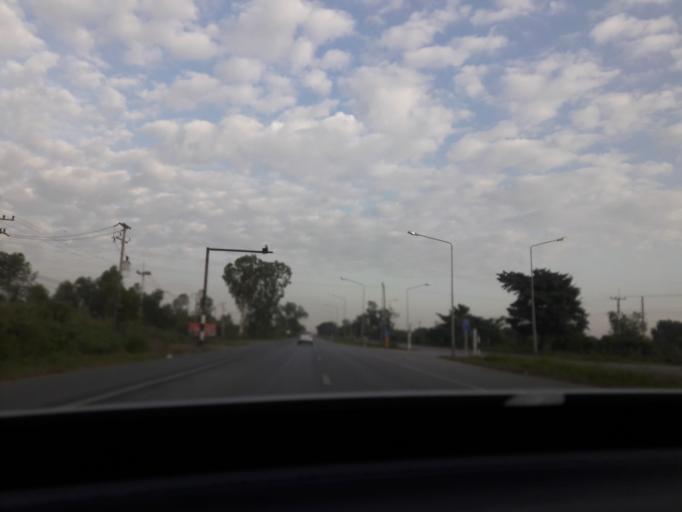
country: TH
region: Phra Nakhon Si Ayutthaya
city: Bang Pa-in
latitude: 14.2829
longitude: 100.5269
